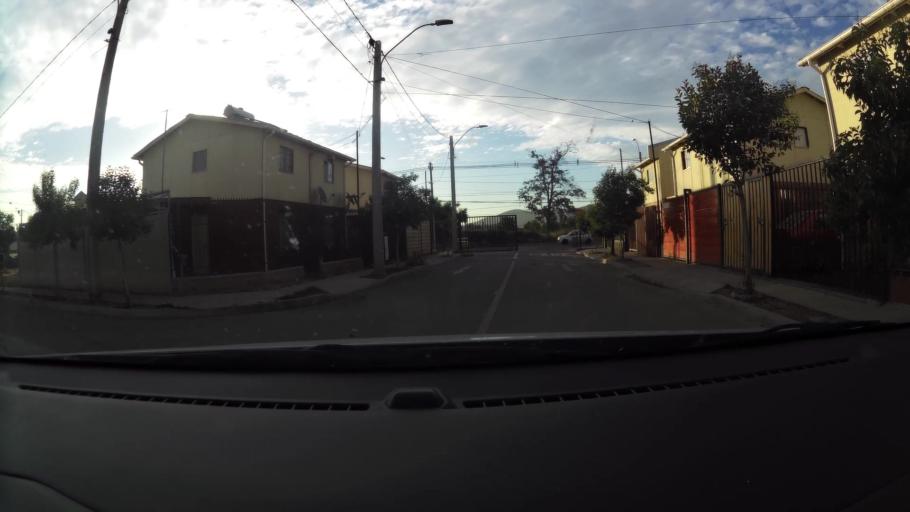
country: CL
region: Santiago Metropolitan
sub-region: Provincia de Maipo
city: San Bernardo
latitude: -33.6230
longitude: -70.6910
